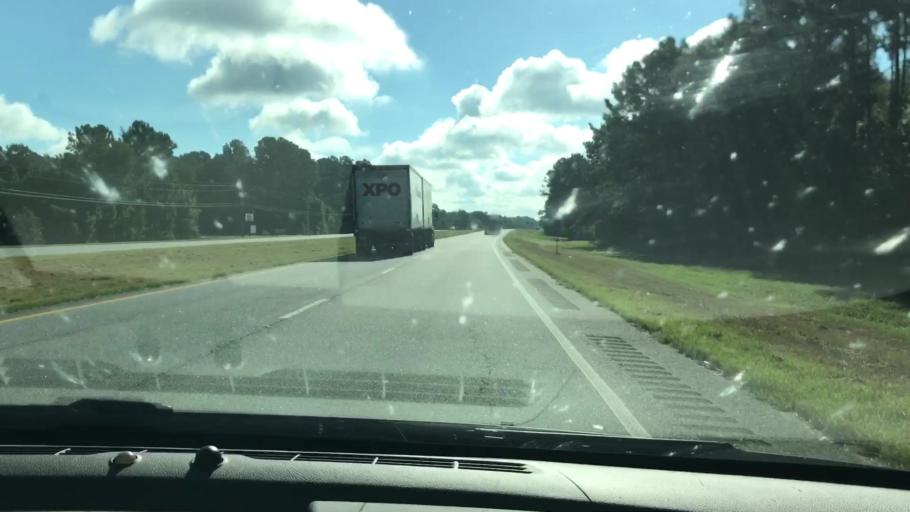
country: US
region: Georgia
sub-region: Dougherty County
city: Putney
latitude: 31.5547
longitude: -83.9907
